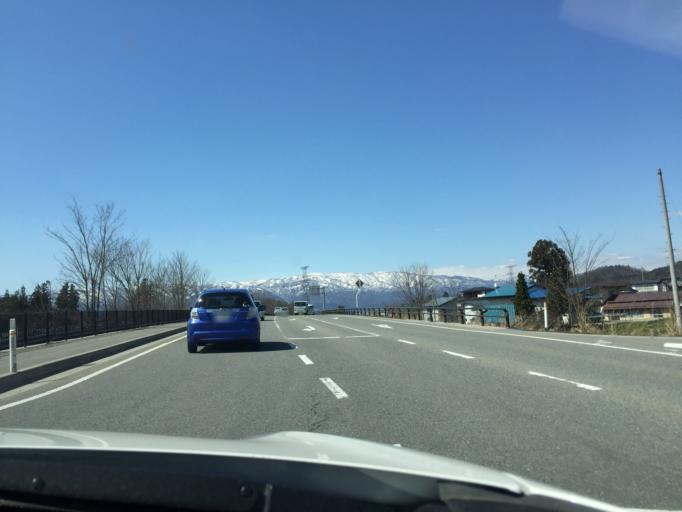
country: JP
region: Yamagata
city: Nagai
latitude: 38.0598
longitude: 140.0547
